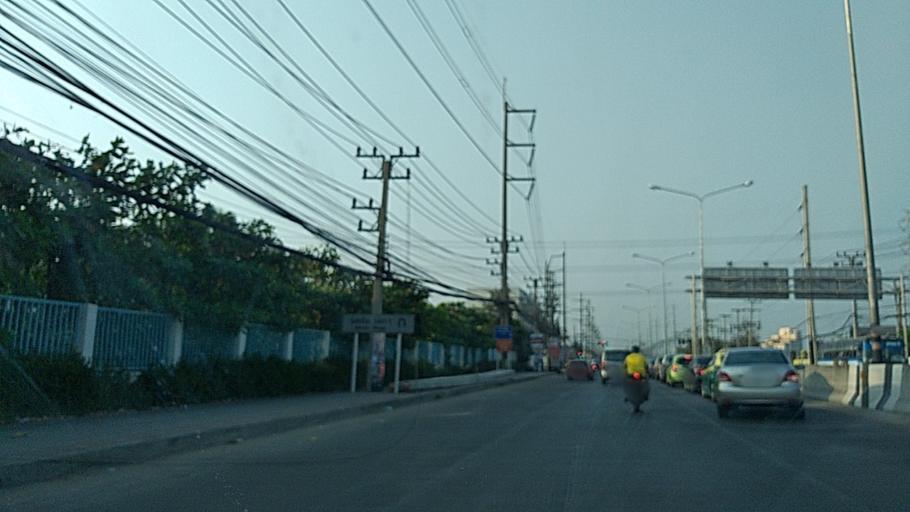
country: TH
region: Phra Nakhon Si Ayutthaya
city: Ban Bang Kadi Pathum Thani
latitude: 13.9737
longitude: 100.5506
